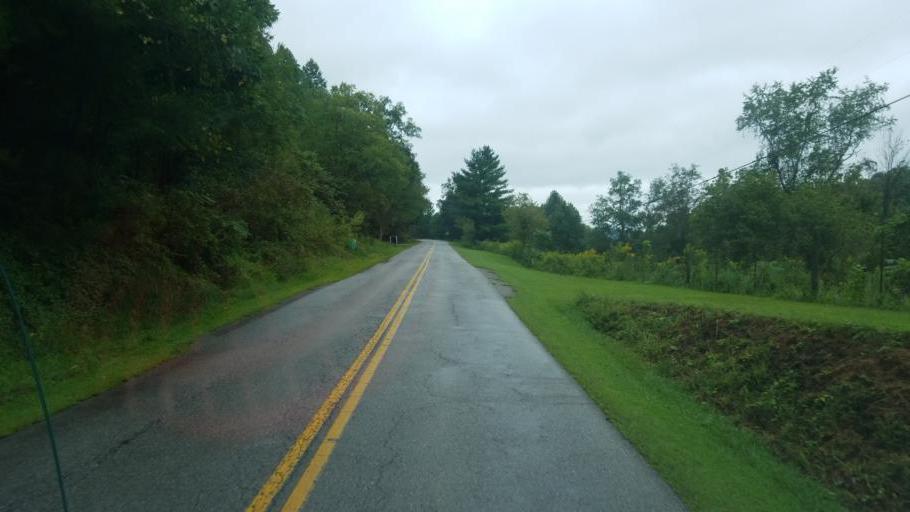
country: US
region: Kentucky
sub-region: Rowan County
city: Morehead
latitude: 38.3621
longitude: -83.5346
